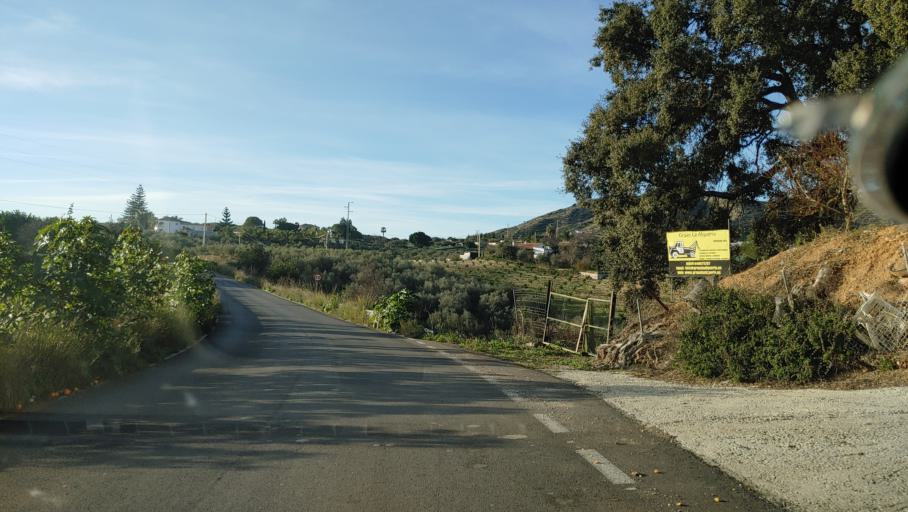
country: ES
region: Andalusia
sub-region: Provincia de Malaga
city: Cartama
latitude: 36.6819
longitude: -4.6328
